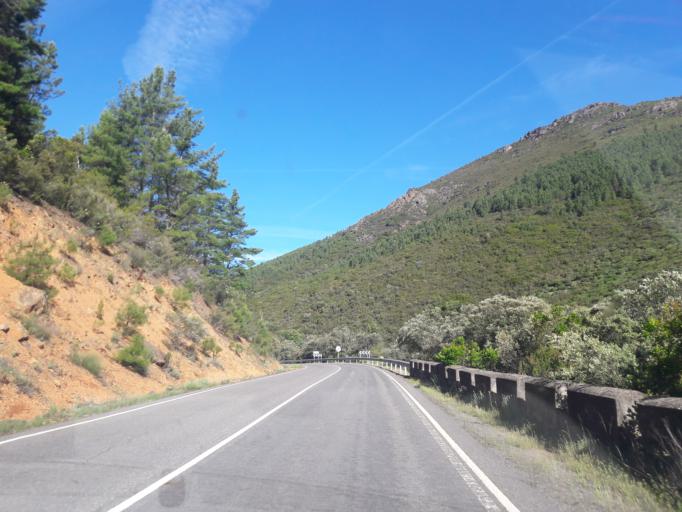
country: ES
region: Castille and Leon
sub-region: Provincia de Salamanca
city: Sotoserrano
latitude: 40.4056
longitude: -6.0569
